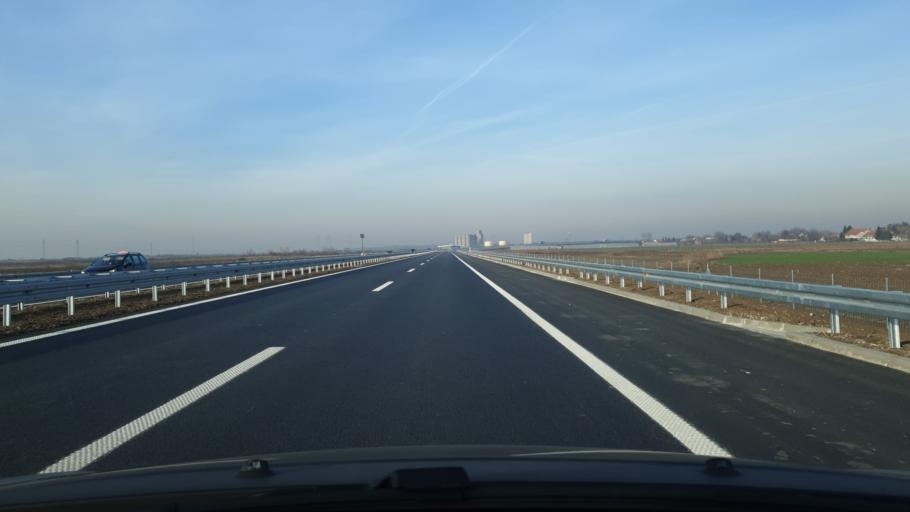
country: RS
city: Boljevci
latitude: 44.7555
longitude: 20.2483
